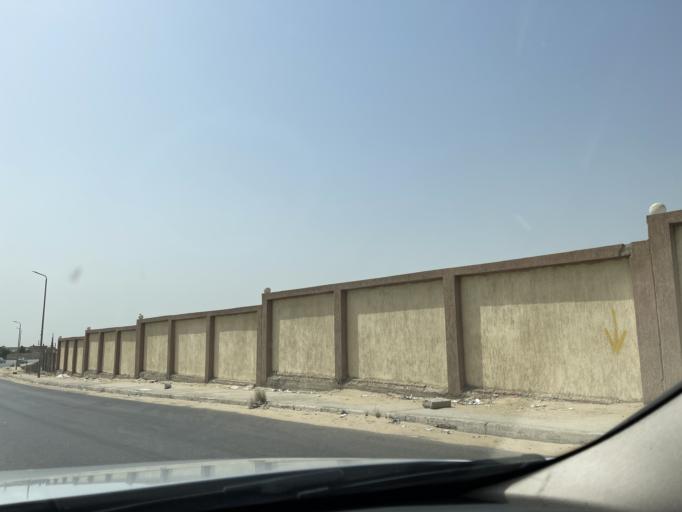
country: EG
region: Muhafazat al Qahirah
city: Cairo
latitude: 30.0245
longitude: 31.3562
